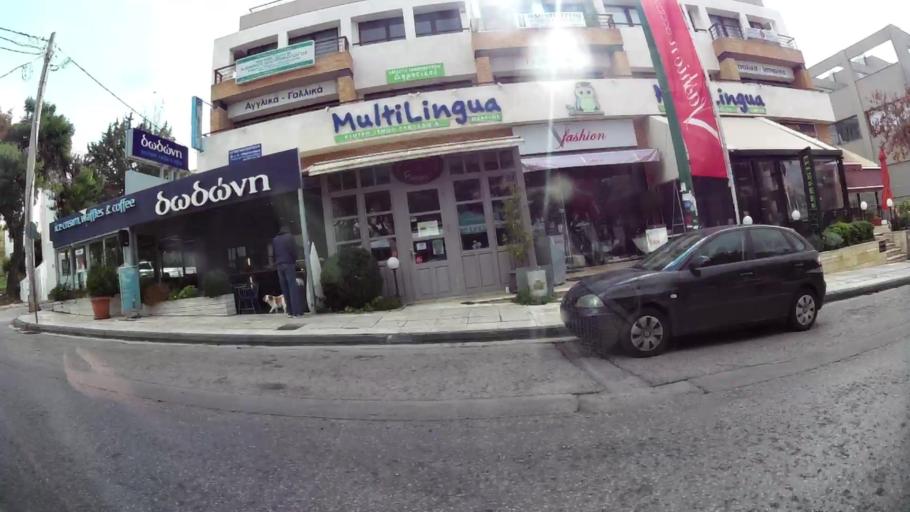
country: GR
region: Attica
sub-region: Nomarchia Athinas
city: Melissia
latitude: 38.0536
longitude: 23.8417
